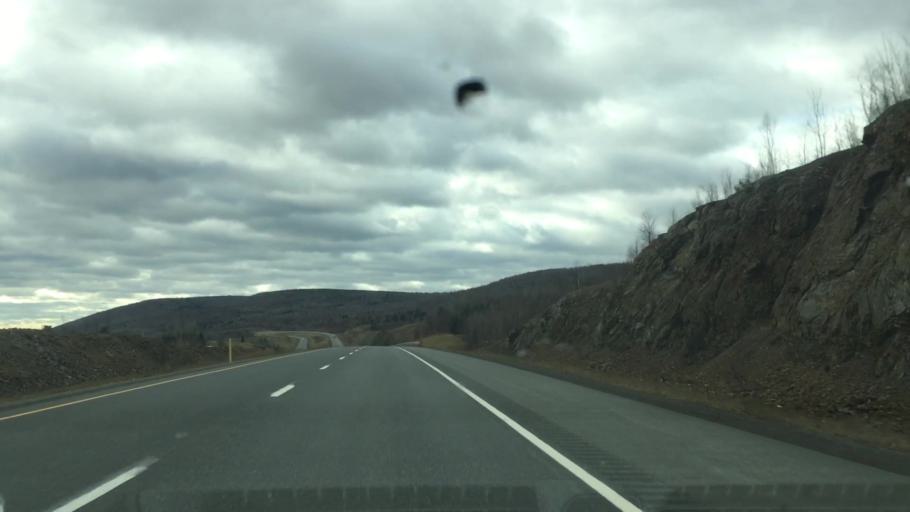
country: US
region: Maine
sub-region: Aroostook County
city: Fort Fairfield
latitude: 46.7139
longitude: -67.7349
